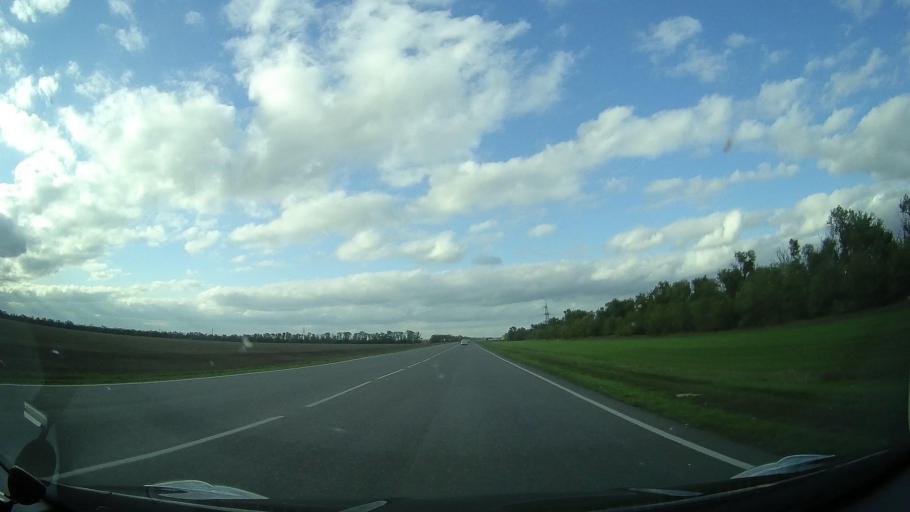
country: RU
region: Rostov
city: Kagal'nitskaya
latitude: 46.9251
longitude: 40.1006
